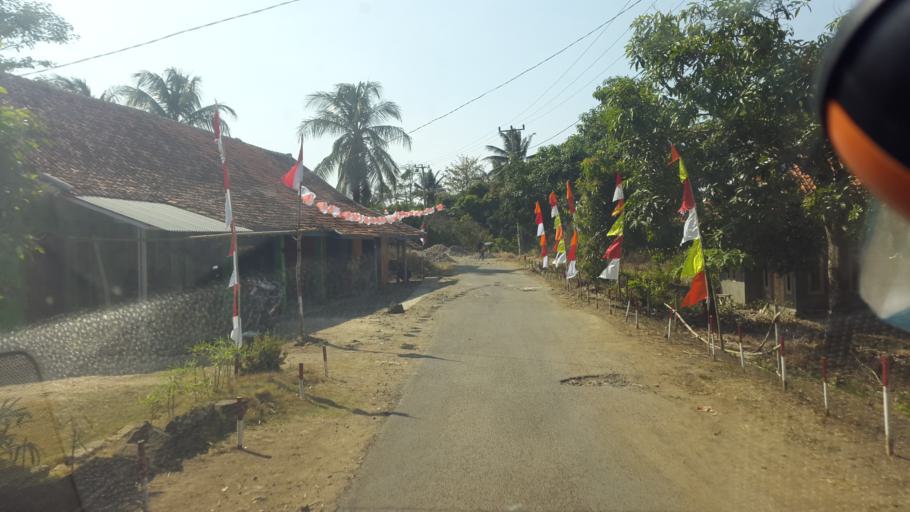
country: ID
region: West Java
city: Simpang
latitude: -7.3043
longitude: 106.4804
